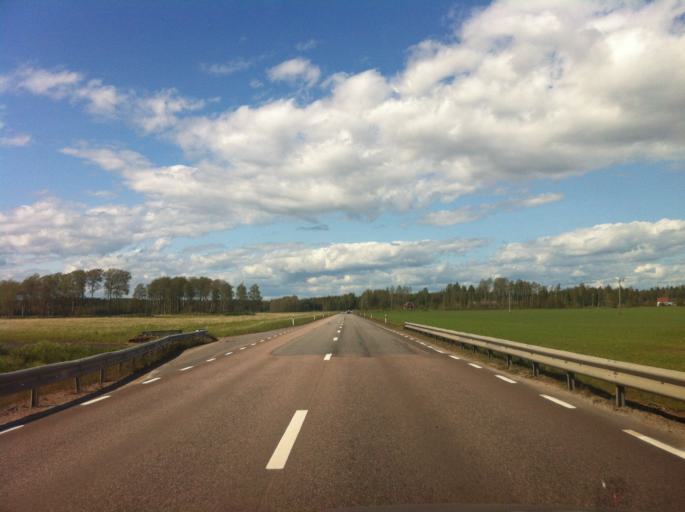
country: SE
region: Vaermland
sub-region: Kristinehamns Kommun
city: Bjorneborg
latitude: 59.1658
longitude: 14.1771
